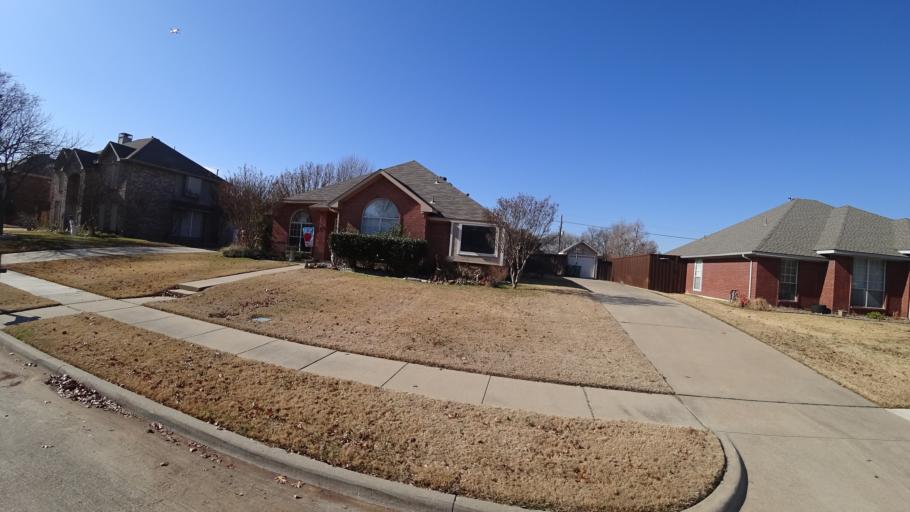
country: US
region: Texas
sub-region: Denton County
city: Lewisville
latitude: 33.0113
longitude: -97.0186
